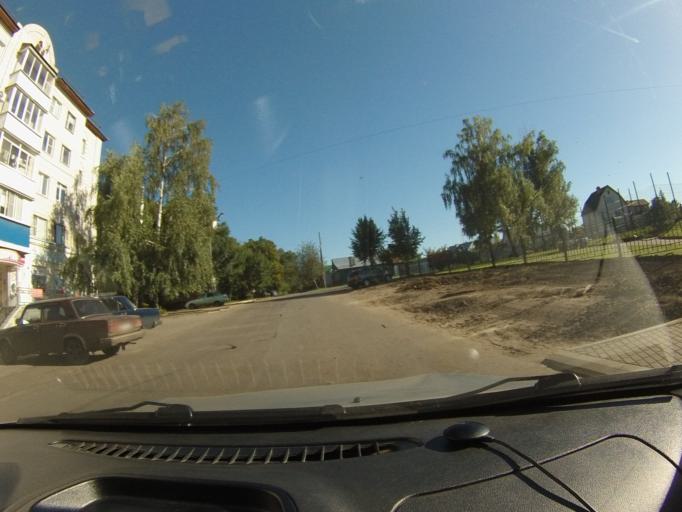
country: RU
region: Tambov
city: Tambov
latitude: 52.7532
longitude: 41.4278
